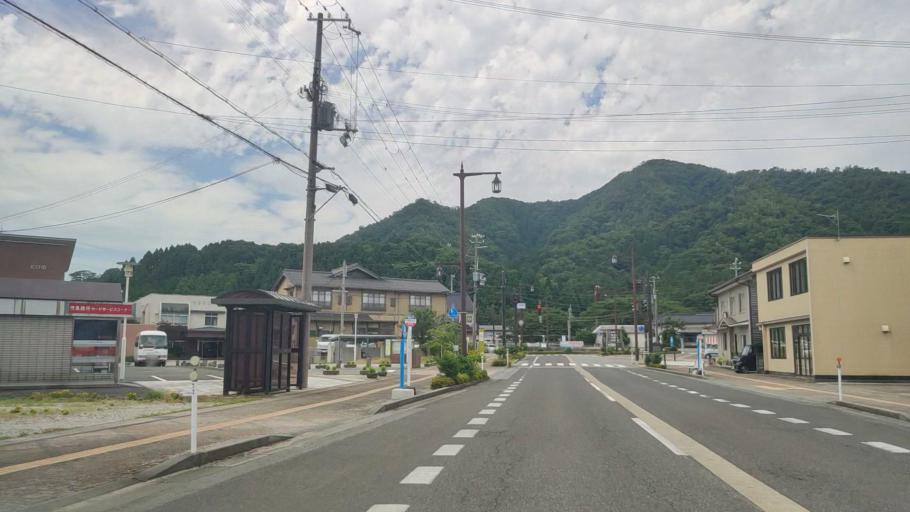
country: JP
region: Hyogo
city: Toyooka
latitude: 35.6508
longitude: 134.7575
